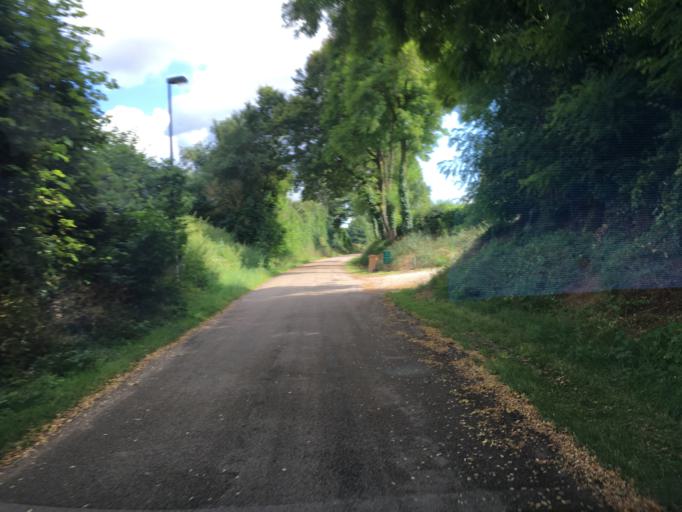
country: FR
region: Bourgogne
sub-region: Departement de l'Yonne
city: Aillant-sur-Tholon
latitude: 47.8335
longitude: 3.3706
